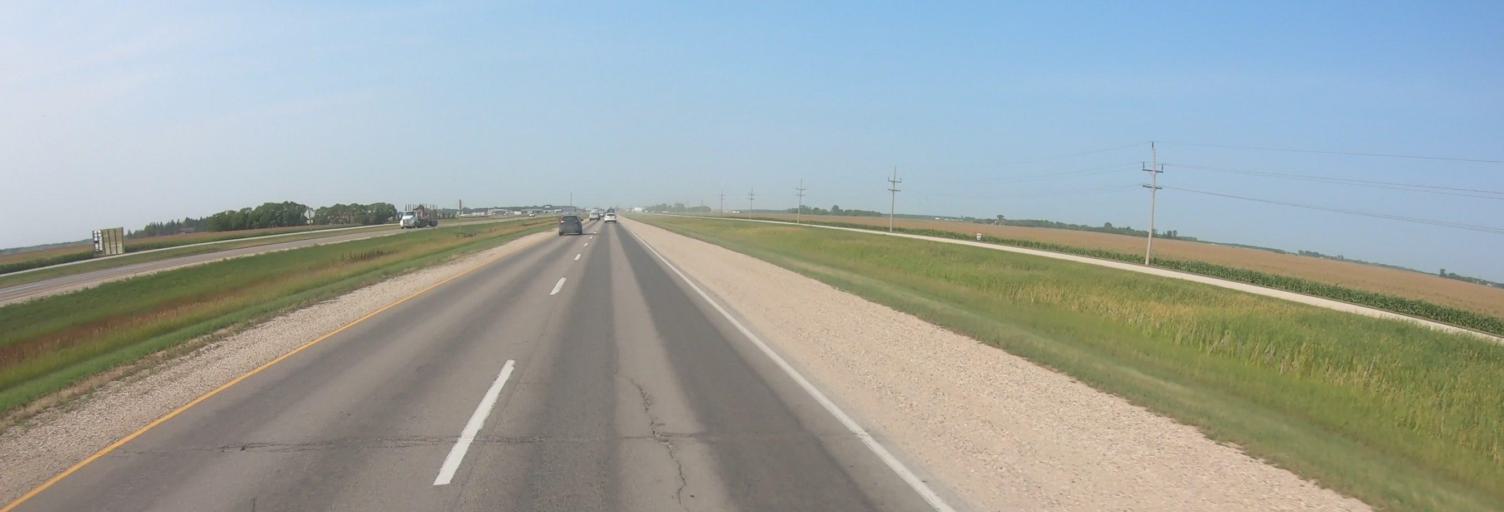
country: CA
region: Manitoba
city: Steinbach
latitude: 49.5845
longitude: -96.6874
